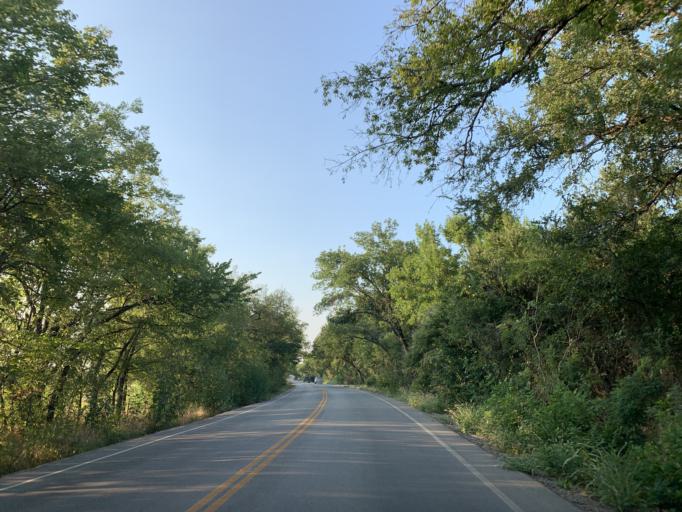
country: US
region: Texas
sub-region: Tarrant County
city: Hurst
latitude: 32.7837
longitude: -97.1779
